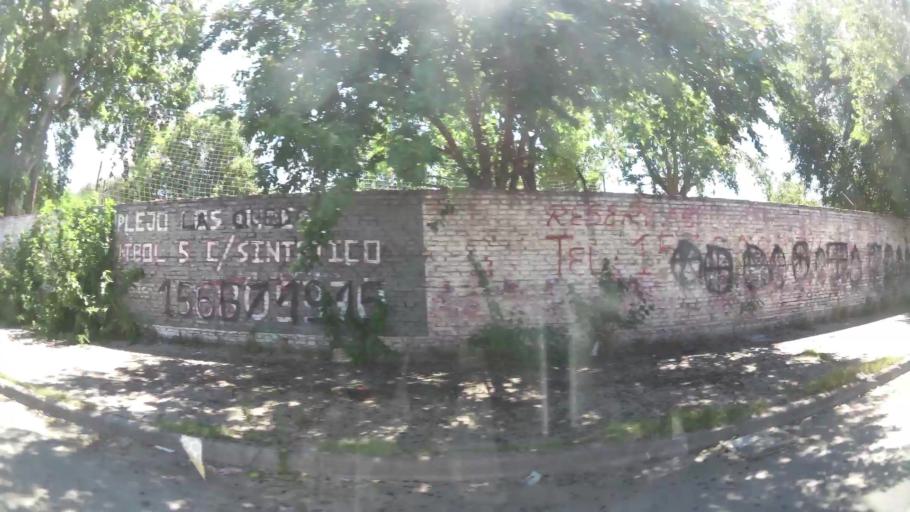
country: AR
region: Cordoba
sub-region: Departamento de Capital
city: Cordoba
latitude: -31.3882
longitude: -64.1923
